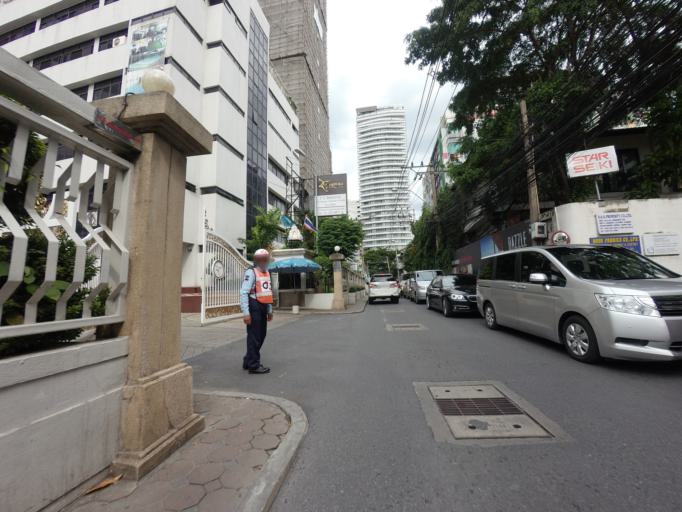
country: TH
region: Bangkok
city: Din Daeng
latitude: 13.7457
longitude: 100.5551
